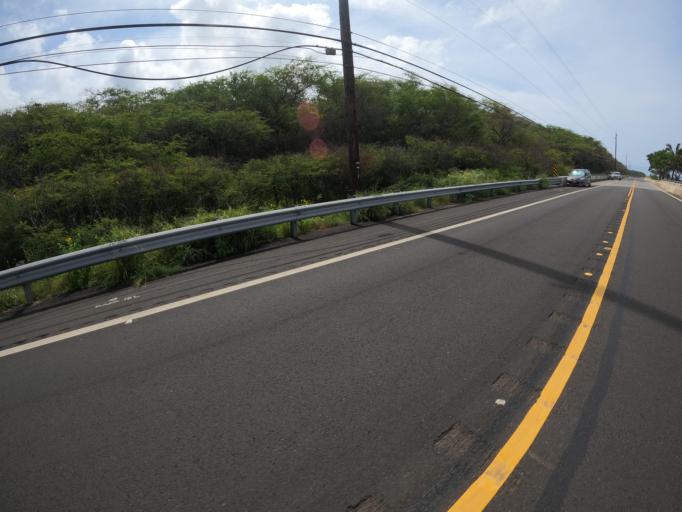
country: US
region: Hawaii
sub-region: Honolulu County
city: Makaha Valley
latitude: 21.5061
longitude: -158.2286
